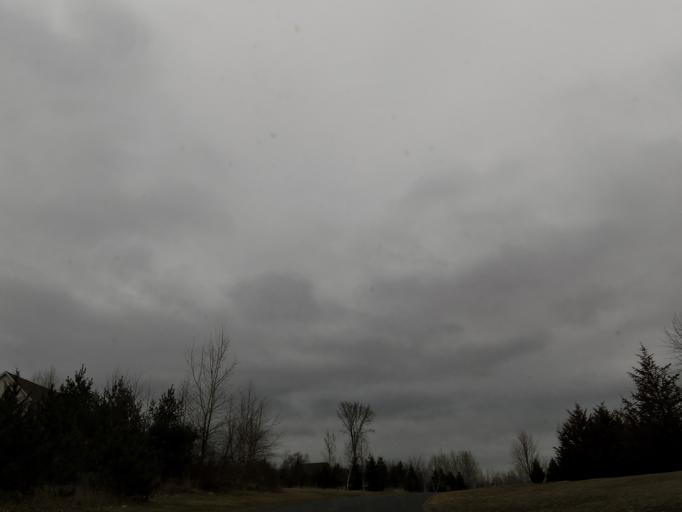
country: US
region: Minnesota
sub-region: Washington County
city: Lakeland
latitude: 44.9671
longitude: -92.8084
